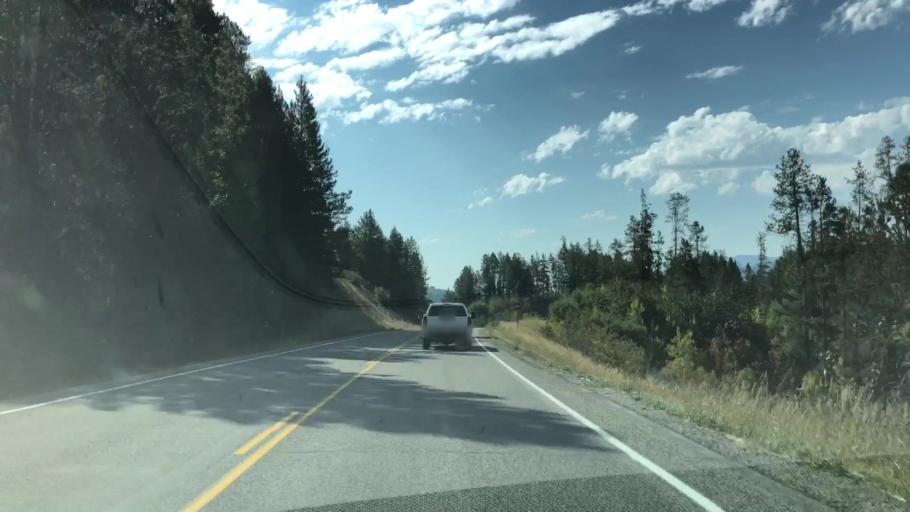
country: US
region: Idaho
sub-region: Teton County
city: Victor
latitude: 43.2881
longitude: -111.1217
